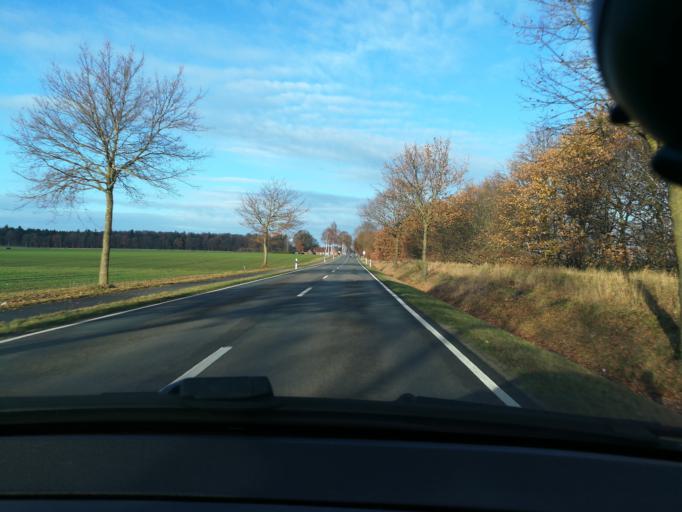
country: DE
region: Lower Saxony
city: Schwaforden
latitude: 52.7183
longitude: 8.8145
